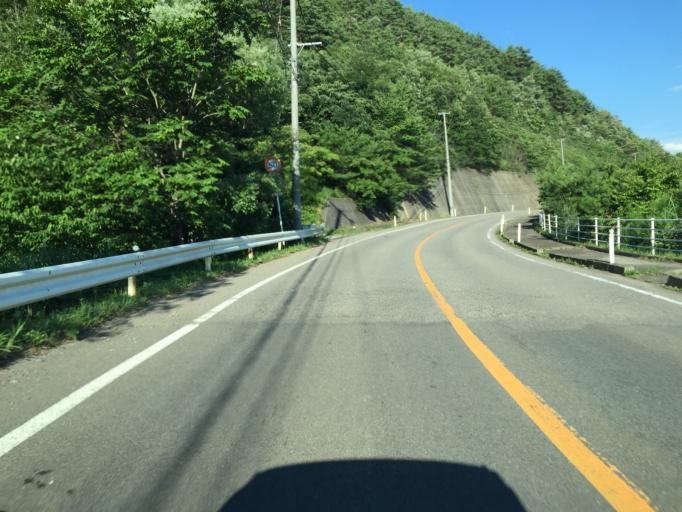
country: JP
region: Miyagi
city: Shiroishi
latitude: 37.9820
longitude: 140.4785
